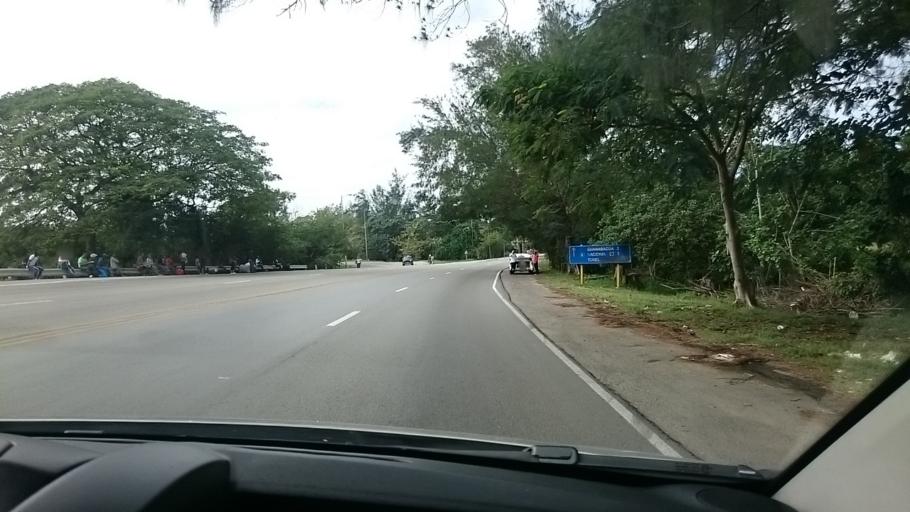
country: CU
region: La Habana
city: Alamar
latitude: 23.1454
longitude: -82.2835
